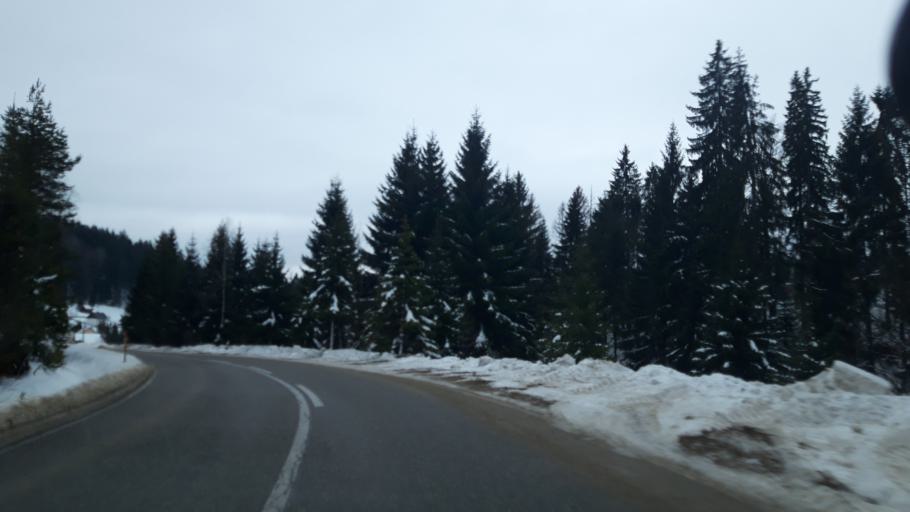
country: BA
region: Republika Srpska
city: Han Pijesak
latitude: 44.1228
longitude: 18.9650
